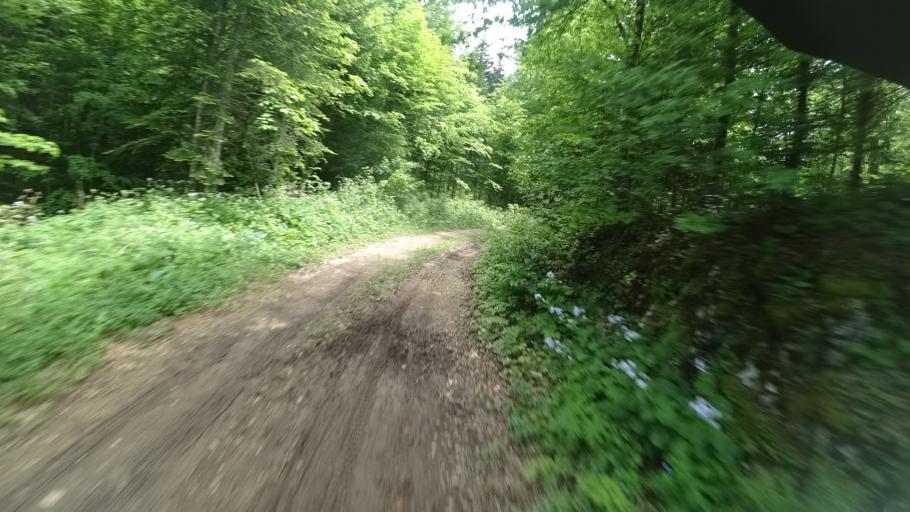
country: HR
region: Zadarska
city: Gracac
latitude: 44.4810
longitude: 15.8817
